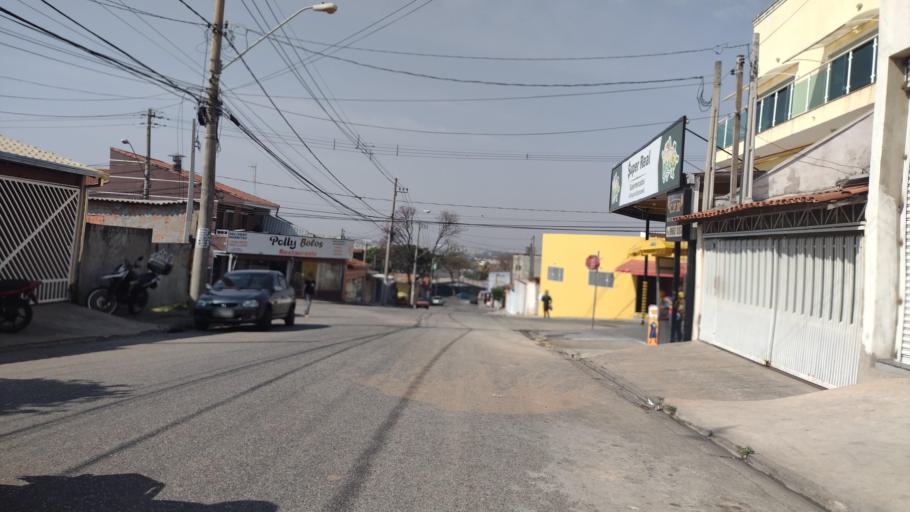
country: BR
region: Sao Paulo
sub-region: Sorocaba
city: Sorocaba
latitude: -23.4311
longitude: -47.4638
